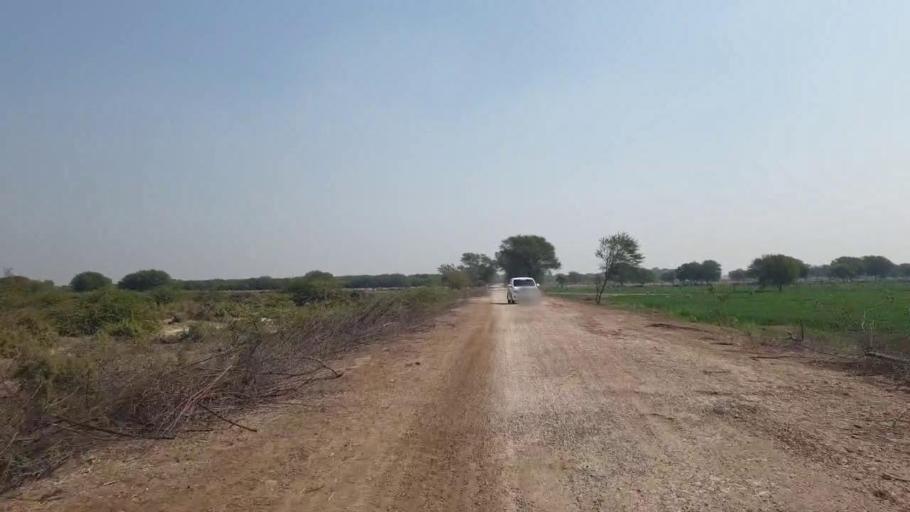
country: PK
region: Sindh
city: Chambar
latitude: 25.3521
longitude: 68.9246
